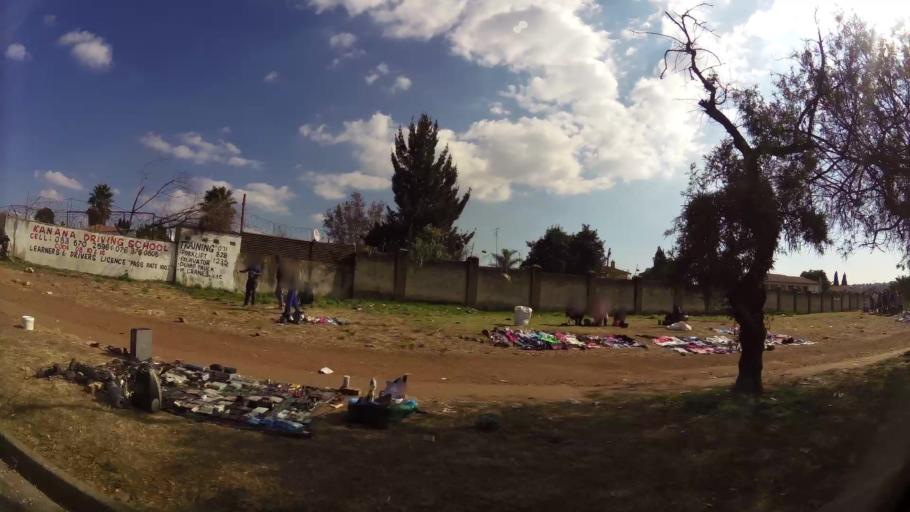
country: ZA
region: Gauteng
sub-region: Ekurhuleni Metropolitan Municipality
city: Germiston
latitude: -26.1891
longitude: 28.1693
